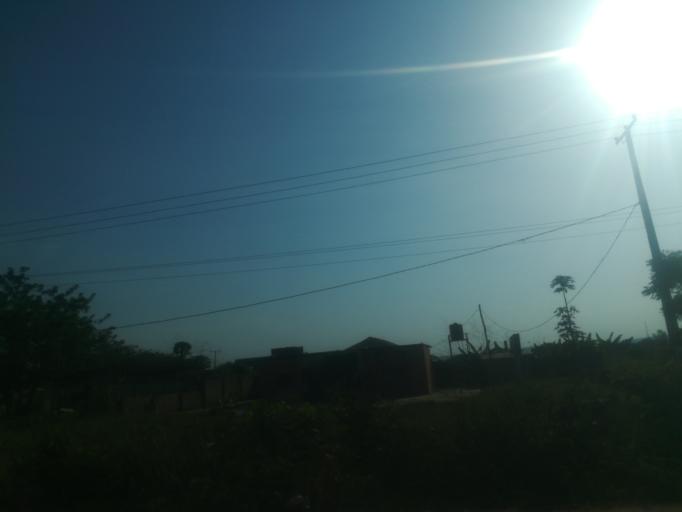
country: NG
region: Ogun
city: Abeokuta
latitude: 7.1782
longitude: 3.2856
